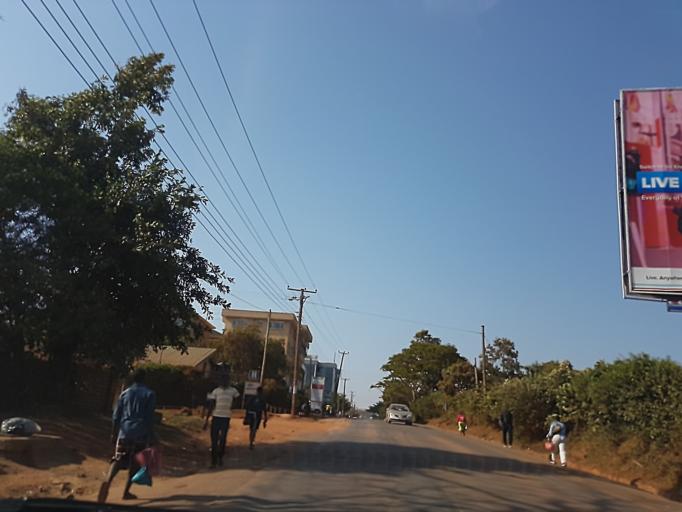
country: UG
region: Central Region
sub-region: Wakiso District
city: Kireka
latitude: 0.3512
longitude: 32.6156
